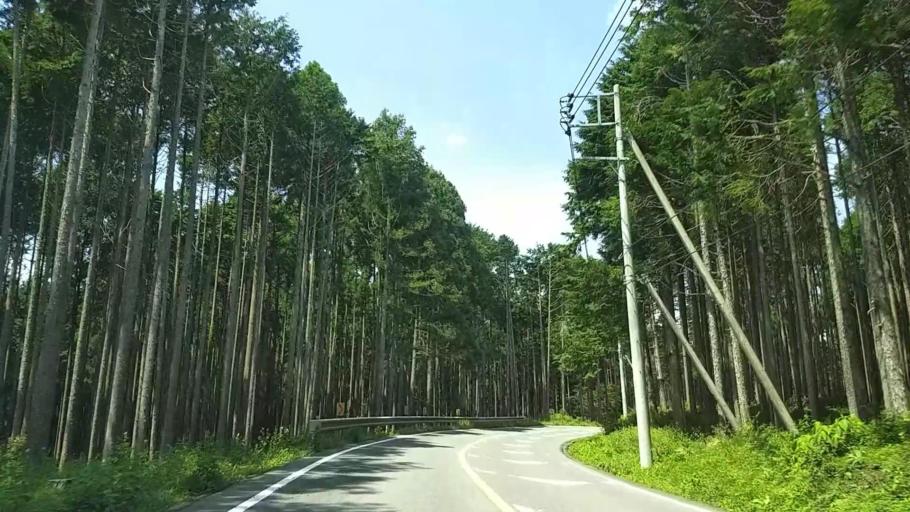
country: JP
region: Shizuoka
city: Fujinomiya
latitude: 35.2949
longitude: 138.6341
